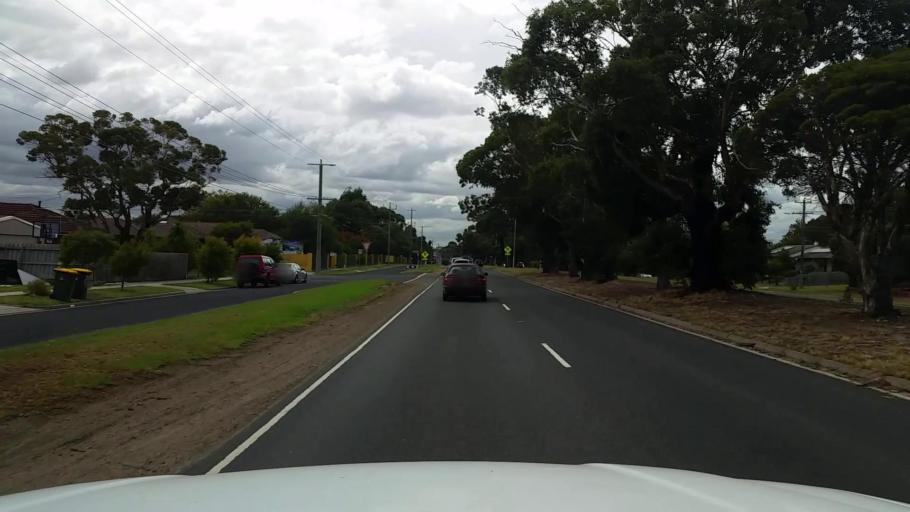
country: AU
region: Victoria
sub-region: Frankston
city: Frankston North
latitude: -38.1168
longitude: 145.1512
